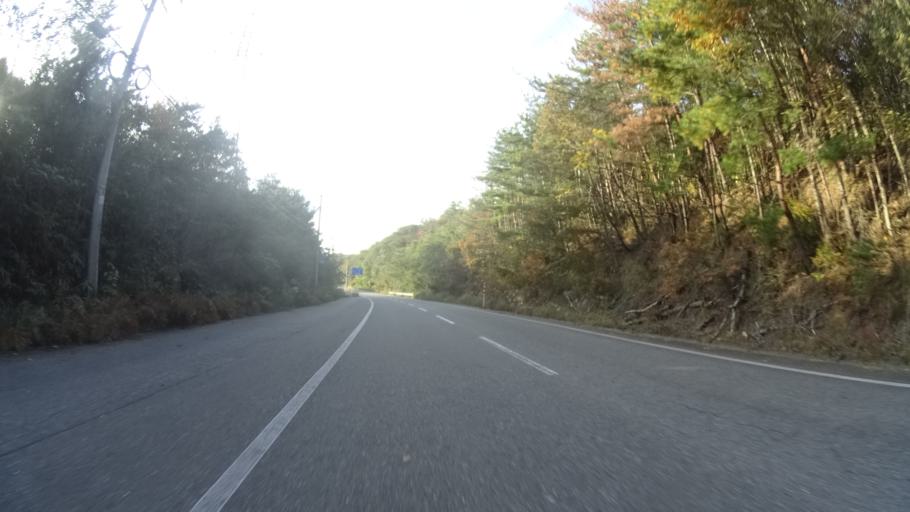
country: JP
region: Ishikawa
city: Hakui
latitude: 37.0704
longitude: 136.7450
